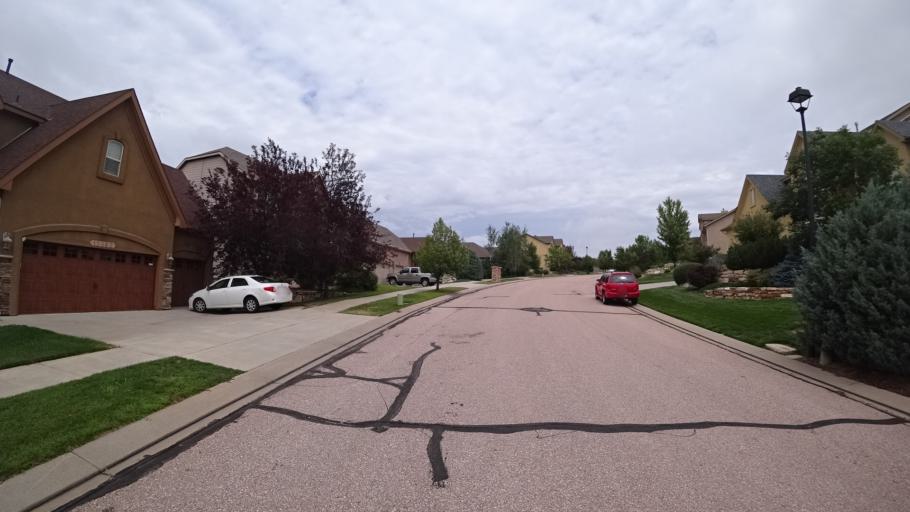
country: US
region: Colorado
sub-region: El Paso County
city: Gleneagle
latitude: 39.0147
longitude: -104.7989
